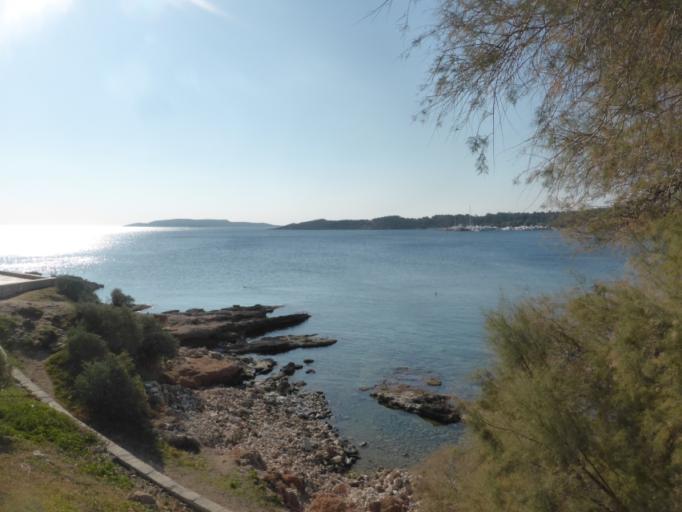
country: GR
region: Attica
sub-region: Nomarchia Anatolikis Attikis
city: Vouliagmeni
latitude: 37.8086
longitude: 23.7828
